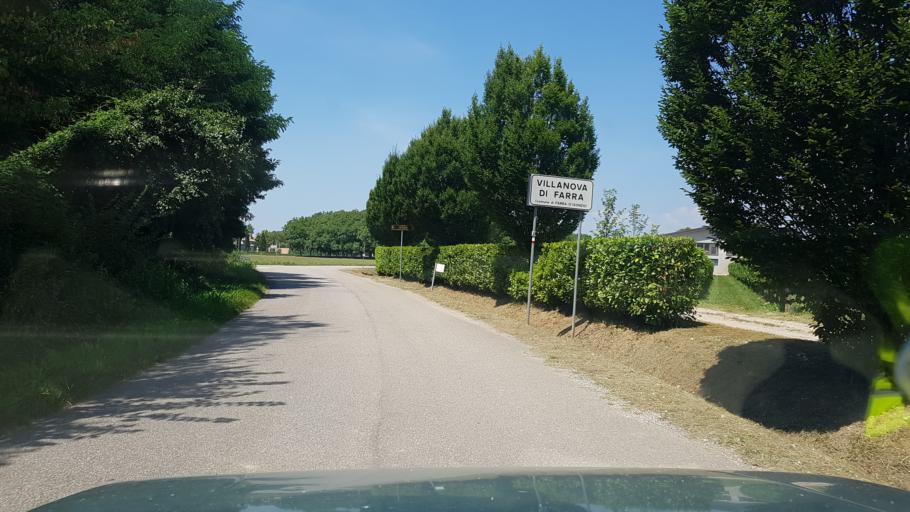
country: IT
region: Friuli Venezia Giulia
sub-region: Provincia di Gorizia
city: Farra d'Isonzo
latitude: 45.9107
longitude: 13.5374
